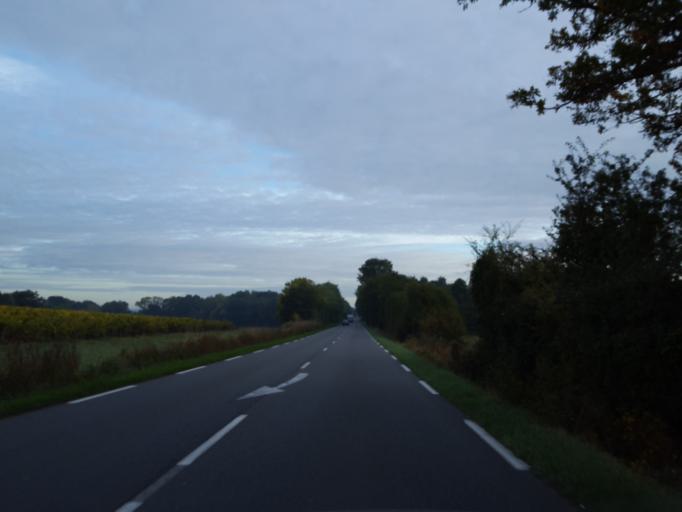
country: FR
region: Pays de la Loire
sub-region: Departement de la Loire-Atlantique
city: Haute-Goulaine
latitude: 47.2089
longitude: -1.4420
